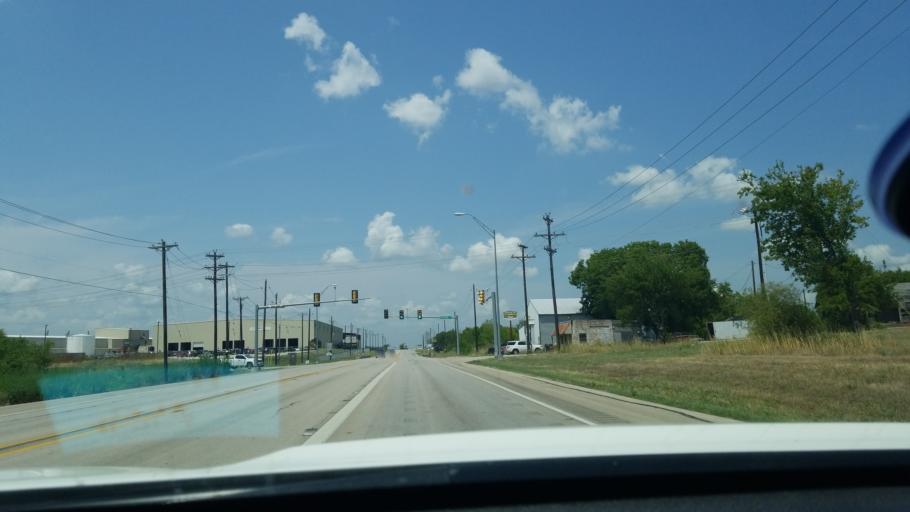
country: US
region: Texas
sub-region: Tarrant County
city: Eagle Mountain
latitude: 32.9344
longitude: -97.4172
